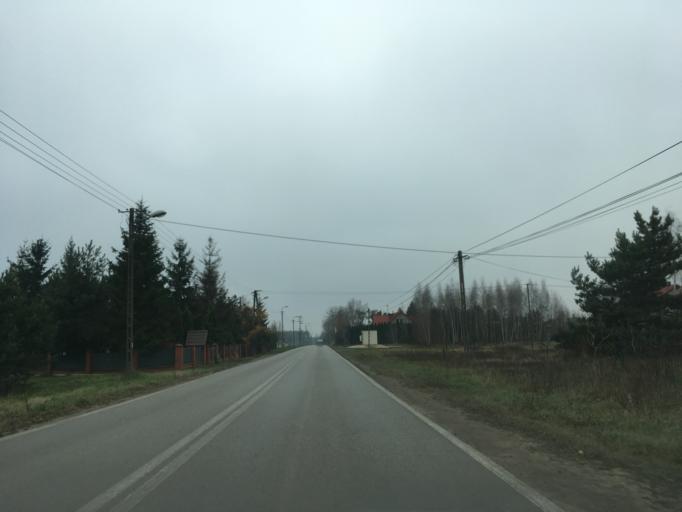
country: PL
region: Masovian Voivodeship
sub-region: Powiat piaseczynski
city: Lesznowola
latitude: 52.0693
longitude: 20.9445
